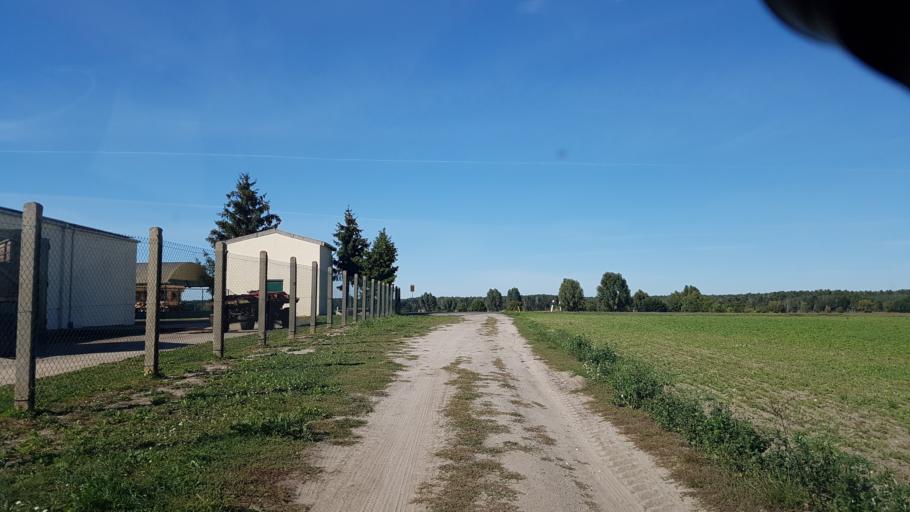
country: DE
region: Brandenburg
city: Ruckersdorf
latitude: 51.5526
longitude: 13.6053
